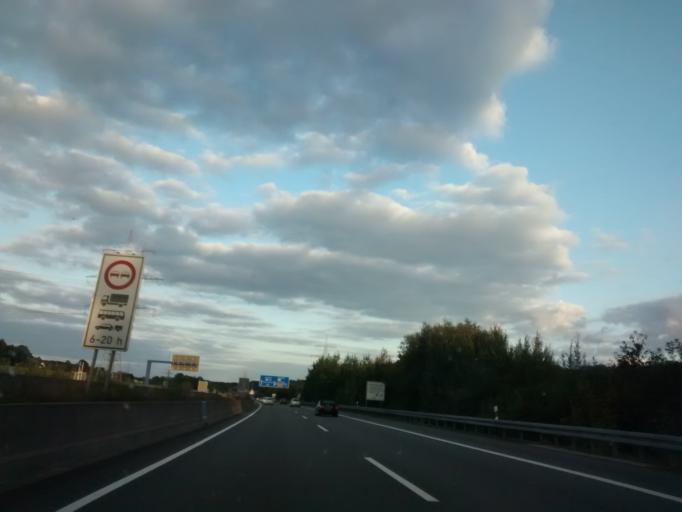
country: DE
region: Lower Saxony
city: Osnabrueck
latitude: 52.2441
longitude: 8.0396
